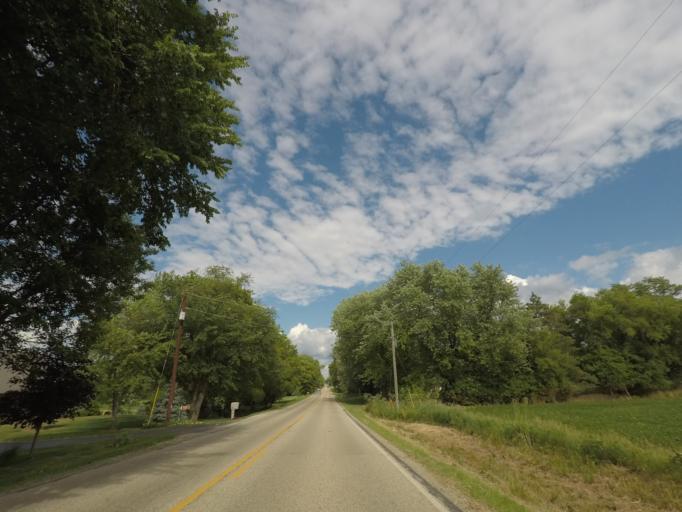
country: US
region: Wisconsin
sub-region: Rock County
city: Janesville
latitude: 42.7011
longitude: -89.0887
